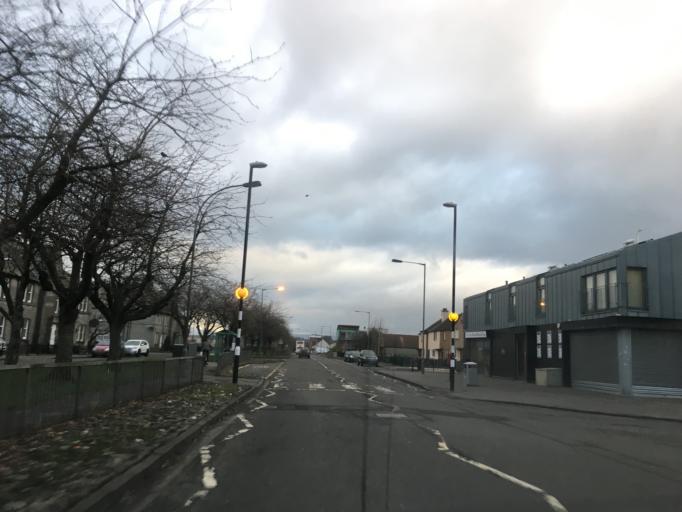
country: GB
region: Scotland
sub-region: Stirling
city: Stirling
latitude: 56.1277
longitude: -3.9547
